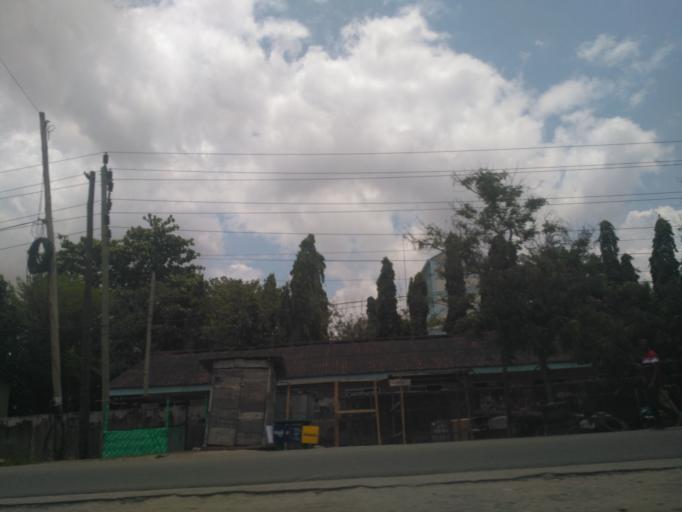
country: TZ
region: Dar es Salaam
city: Dar es Salaam
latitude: -6.8581
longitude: 39.2807
